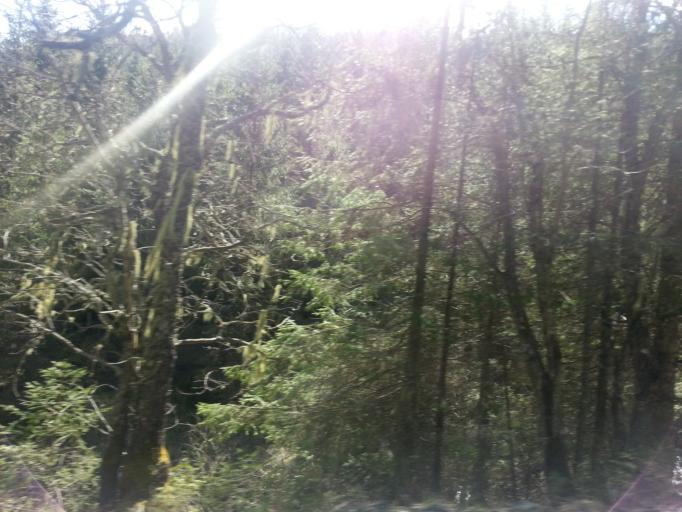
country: NO
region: Nord-Trondelag
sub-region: Levanger
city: Skogn
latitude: 63.5908
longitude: 11.1167
